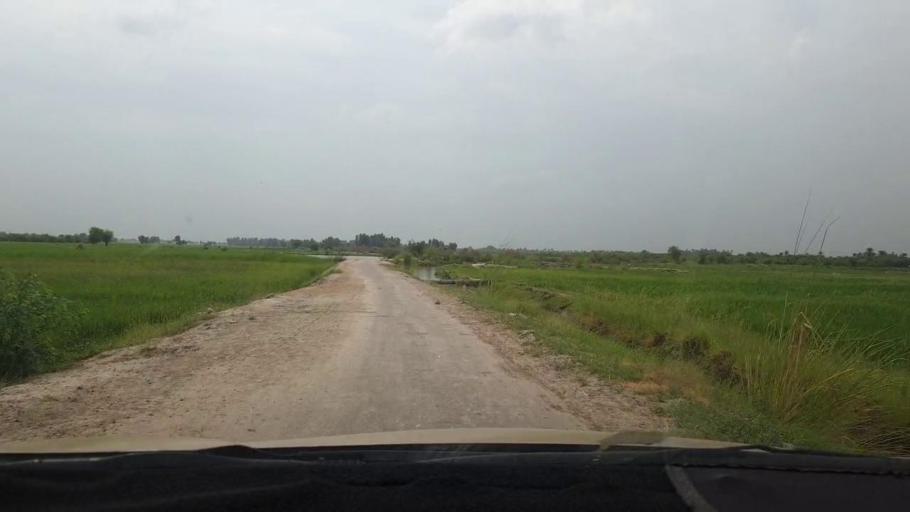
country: PK
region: Sindh
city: Naudero
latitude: 27.6298
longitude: 68.3166
